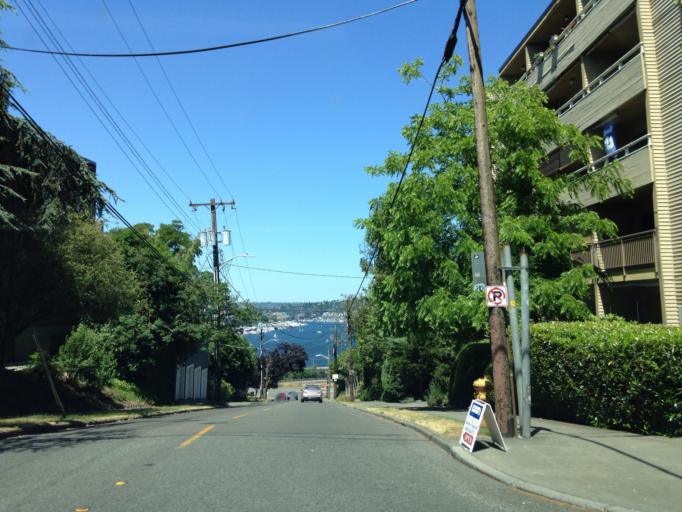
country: US
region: Washington
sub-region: King County
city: Seattle
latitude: 47.6271
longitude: -122.3260
